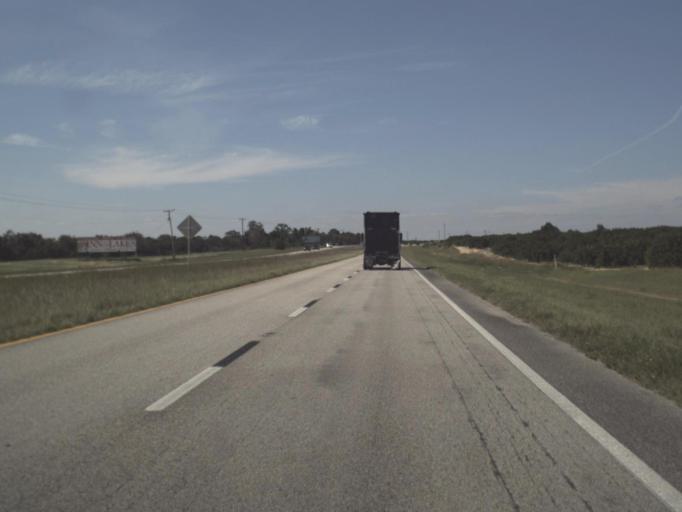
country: US
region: Florida
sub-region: Highlands County
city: Lake Placid
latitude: 27.3281
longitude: -81.3780
